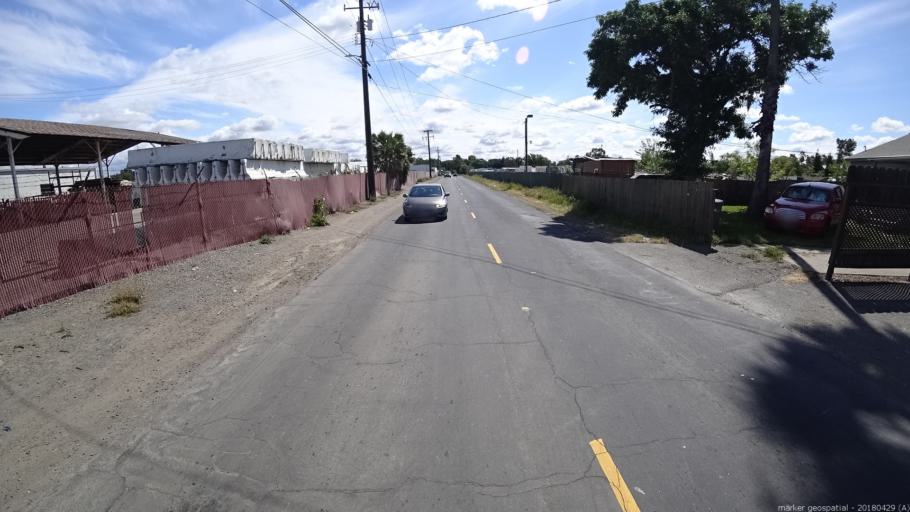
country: US
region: California
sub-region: Yolo County
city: West Sacramento
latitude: 38.5861
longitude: -121.5453
